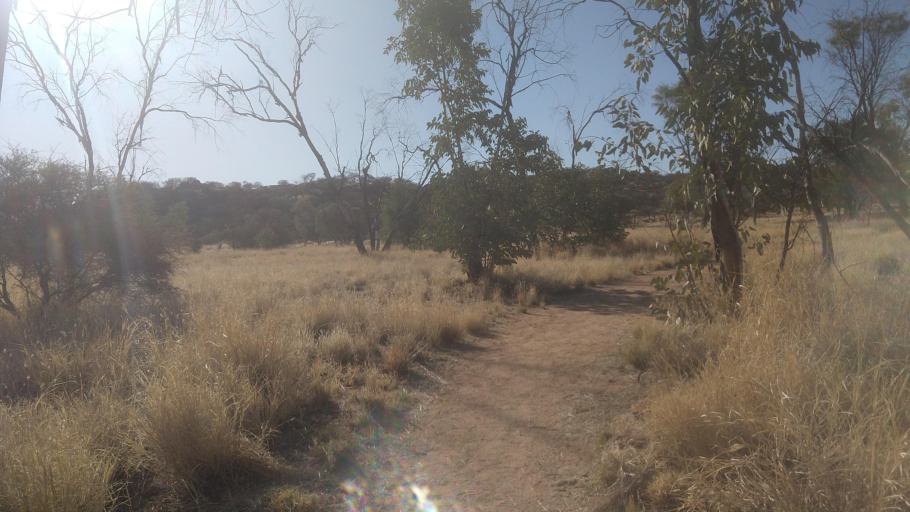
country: AU
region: Northern Territory
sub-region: Alice Springs
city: Alice Springs
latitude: -23.6691
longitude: 133.8832
